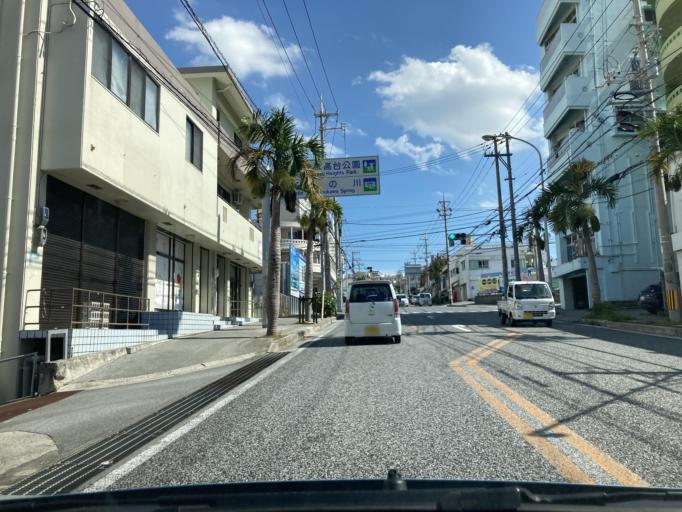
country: JP
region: Okinawa
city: Ginowan
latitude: 26.2673
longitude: 127.7355
